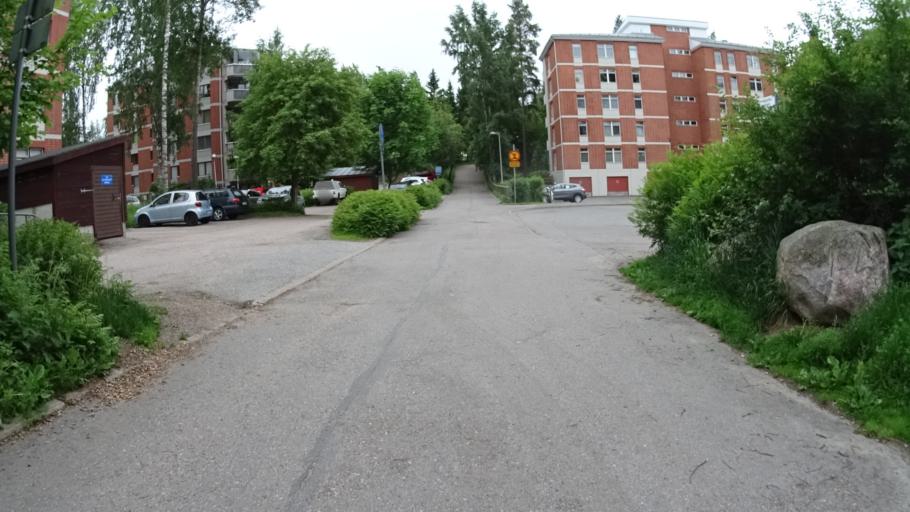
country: FI
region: Uusimaa
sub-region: Helsinki
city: Kilo
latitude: 60.2568
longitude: 24.8072
